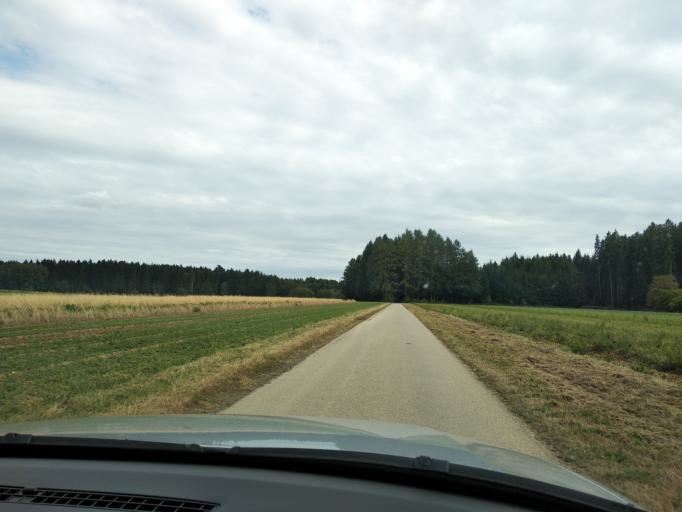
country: DE
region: Bavaria
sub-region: Swabia
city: Kronburg
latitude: 47.9318
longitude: 10.1480
